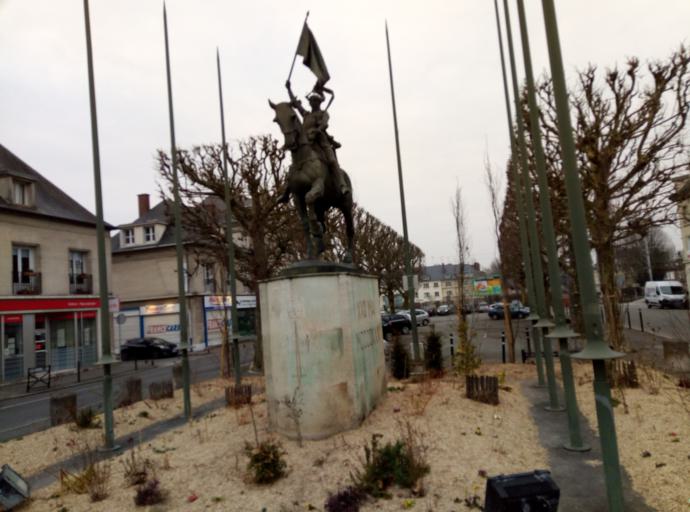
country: FR
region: Picardie
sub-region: Departement de l'Oise
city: Compiegne
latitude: 49.4207
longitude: 2.8225
